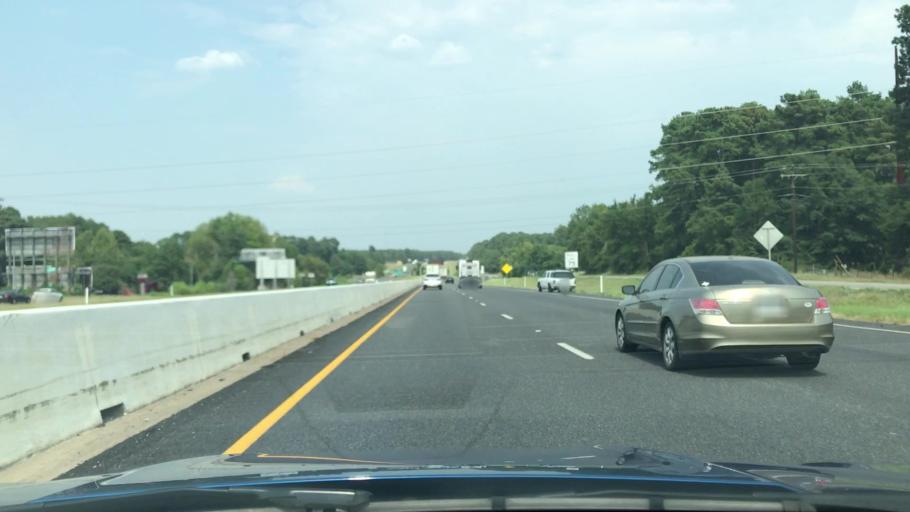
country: US
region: Texas
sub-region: Gregg County
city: Longview
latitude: 32.4517
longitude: -94.7044
